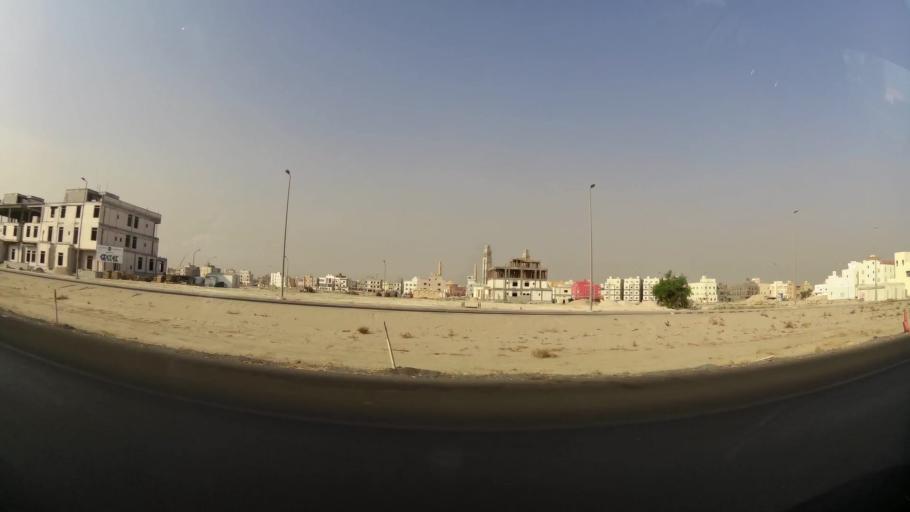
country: KW
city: Al Funaytis
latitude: 29.2212
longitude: 48.1004
